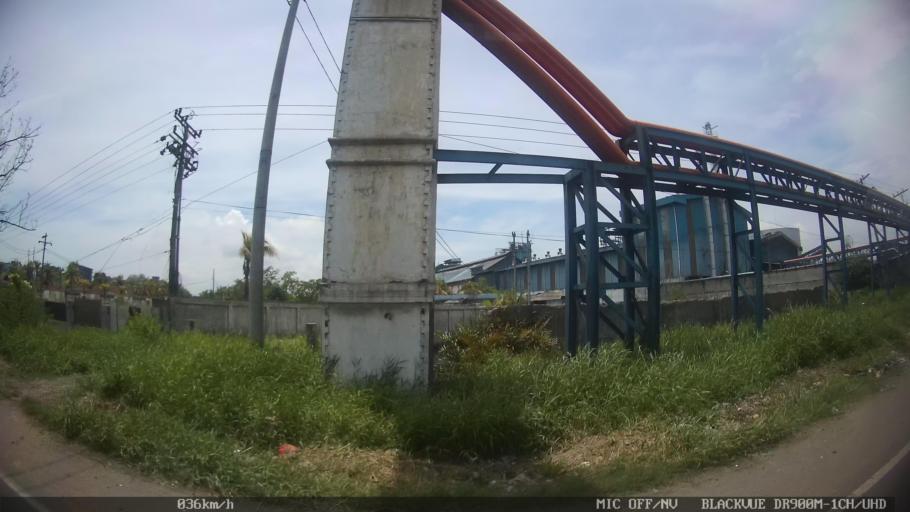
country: ID
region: North Sumatra
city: Belawan
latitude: 3.7809
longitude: 98.6896
